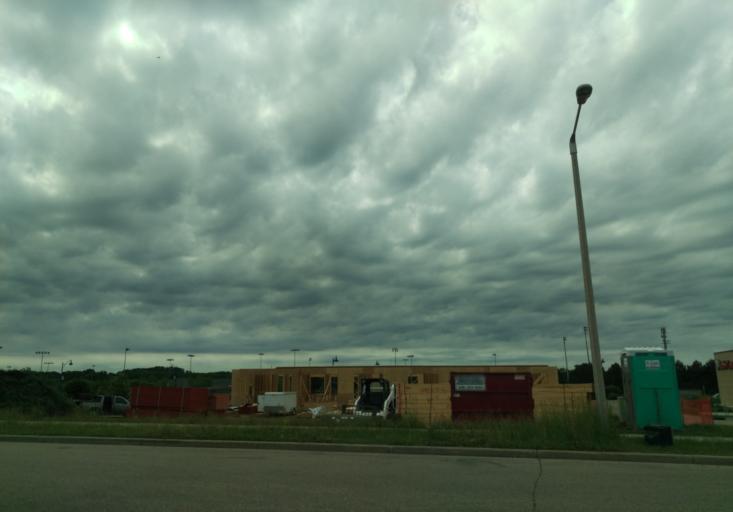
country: US
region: Wisconsin
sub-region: Dane County
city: Verona
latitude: 42.9946
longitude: -89.5215
